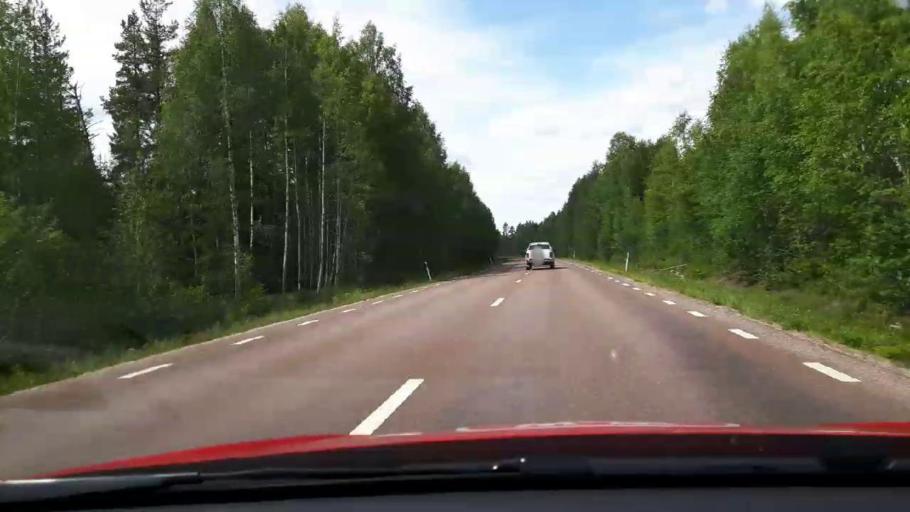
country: SE
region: Jaemtland
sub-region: Harjedalens Kommun
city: Sveg
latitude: 62.0461
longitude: 14.8454
